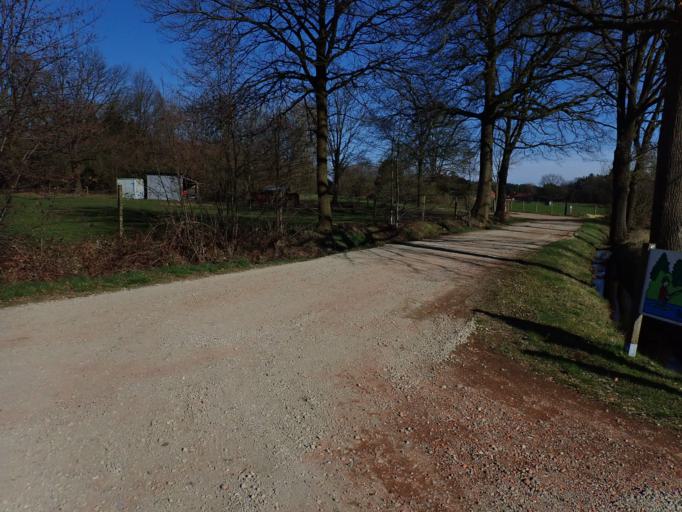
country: BE
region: Flanders
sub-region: Provincie Antwerpen
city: Laakdal
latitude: 51.0580
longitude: 4.9823
